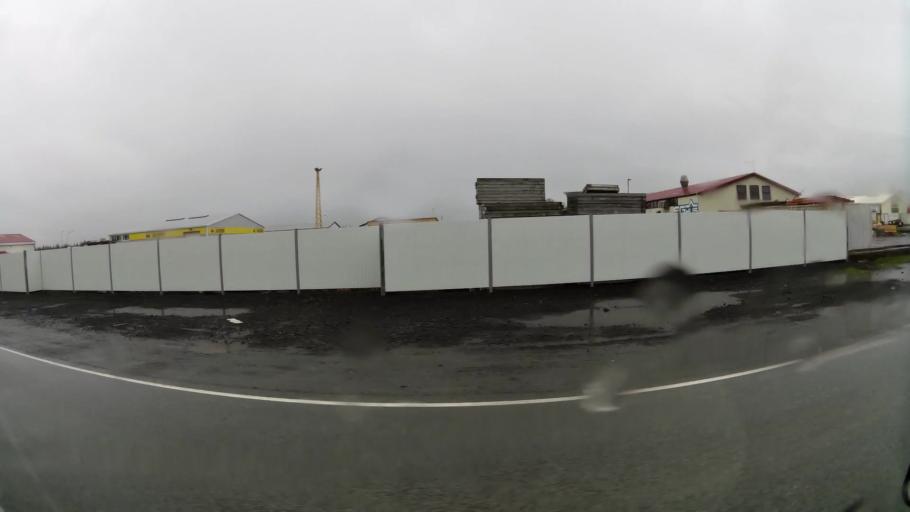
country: IS
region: South
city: Selfoss
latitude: 63.9298
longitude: -21.0203
